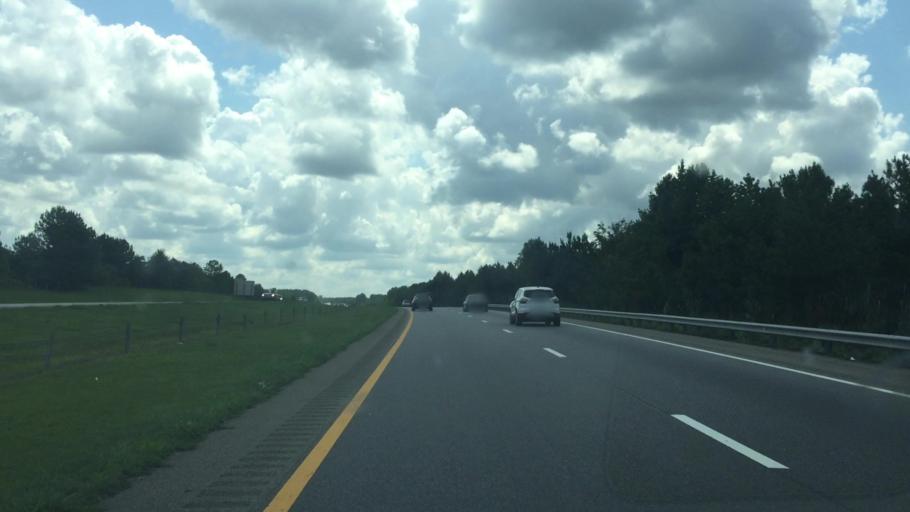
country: US
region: North Carolina
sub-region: Richmond County
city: East Rockingham
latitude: 34.8835
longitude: -79.7842
